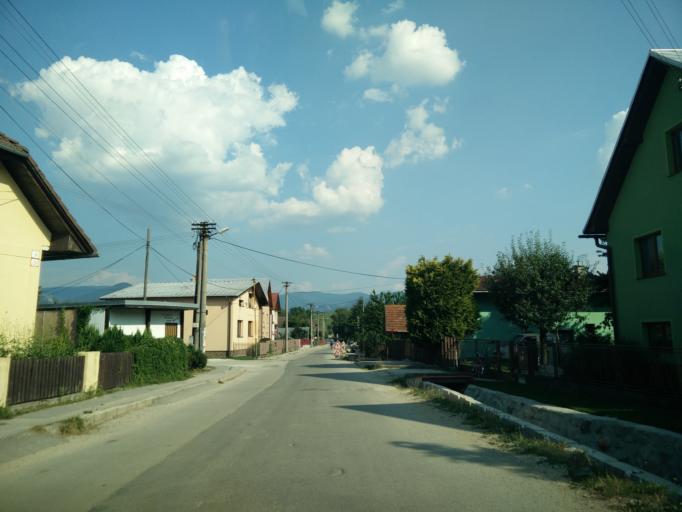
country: SK
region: Zilinsky
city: Rajec
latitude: 49.1207
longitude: 18.6477
